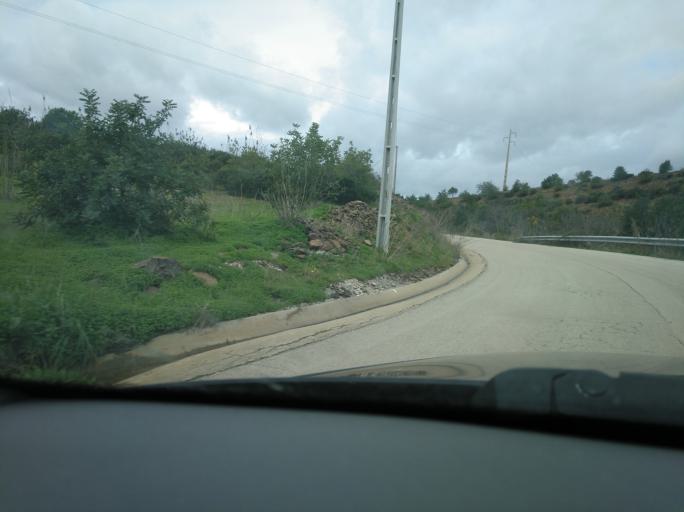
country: PT
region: Faro
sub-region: Castro Marim
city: Castro Marim
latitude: 37.2138
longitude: -7.4858
